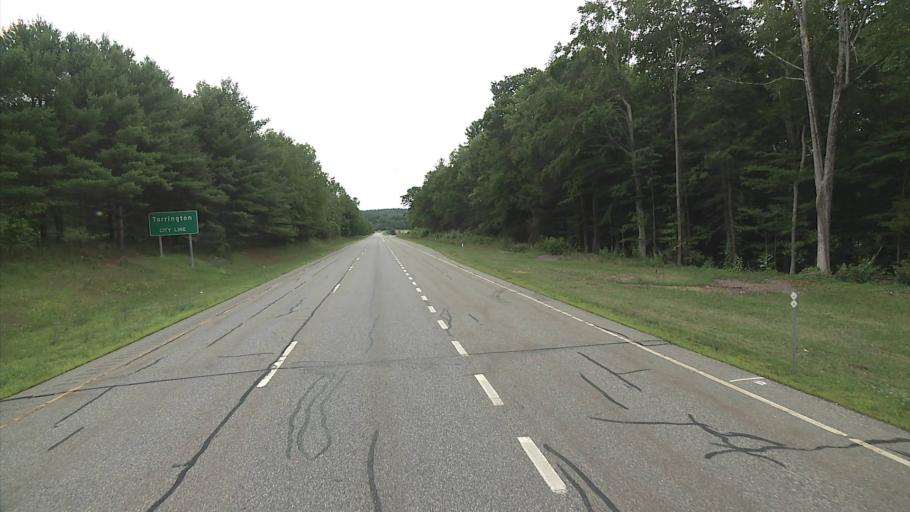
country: US
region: Connecticut
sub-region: Litchfield County
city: Winsted
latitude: 41.8849
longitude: -73.0714
